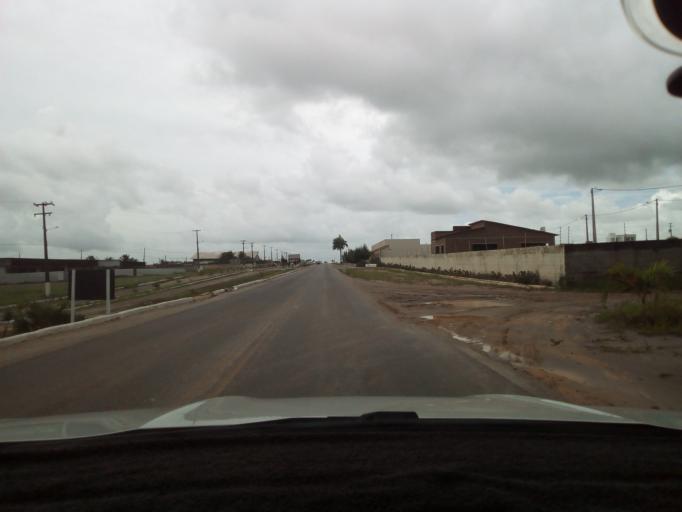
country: BR
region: Paraiba
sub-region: Pedras De Fogo
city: Pedras de Fogo
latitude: -7.4022
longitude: -35.0990
